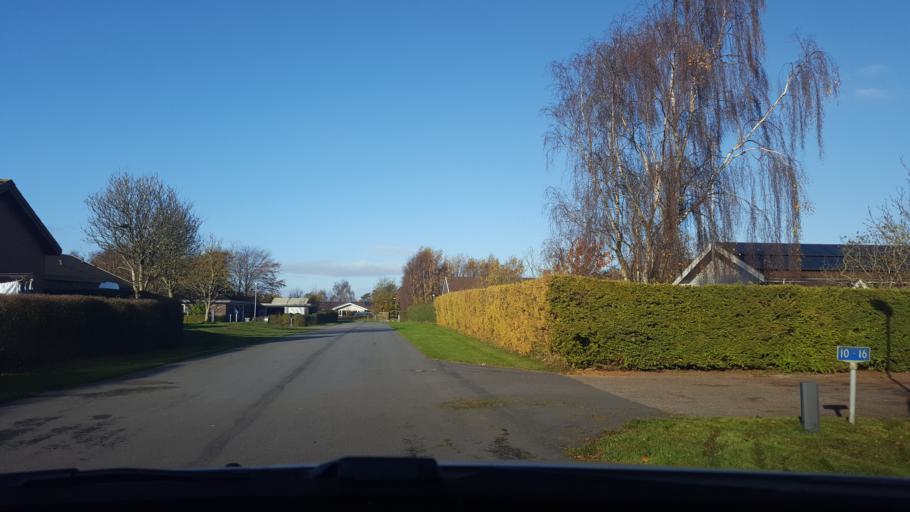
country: DK
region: North Denmark
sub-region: Morso Kommune
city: Nykobing Mors
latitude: 56.7486
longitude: 8.8819
